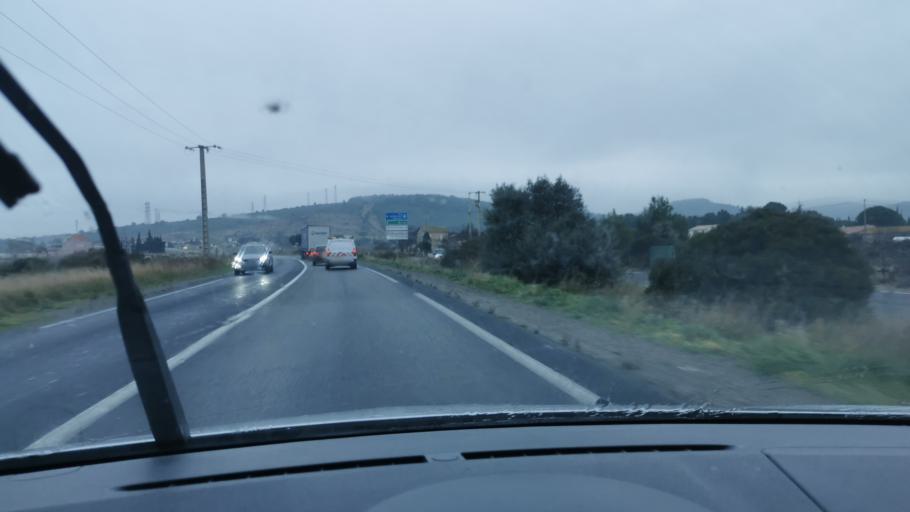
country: FR
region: Languedoc-Roussillon
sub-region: Departement de l'Herault
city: Balaruc-le-Vieux
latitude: 43.4418
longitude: 3.7166
